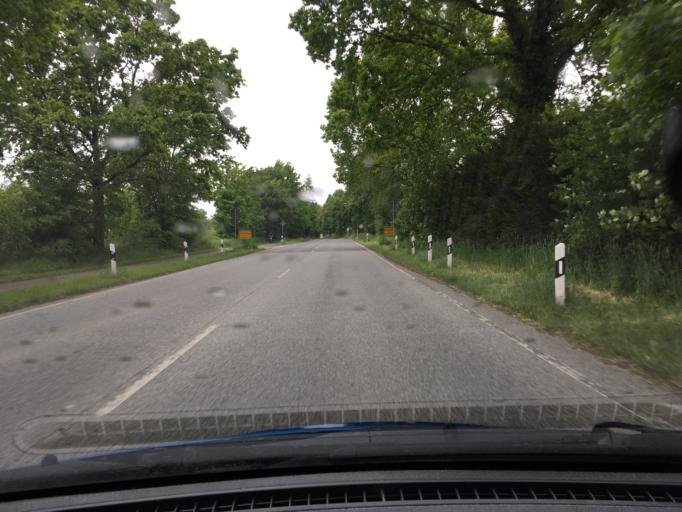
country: DE
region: Schleswig-Holstein
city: Gross Gronau
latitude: 53.7952
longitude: 10.7562
